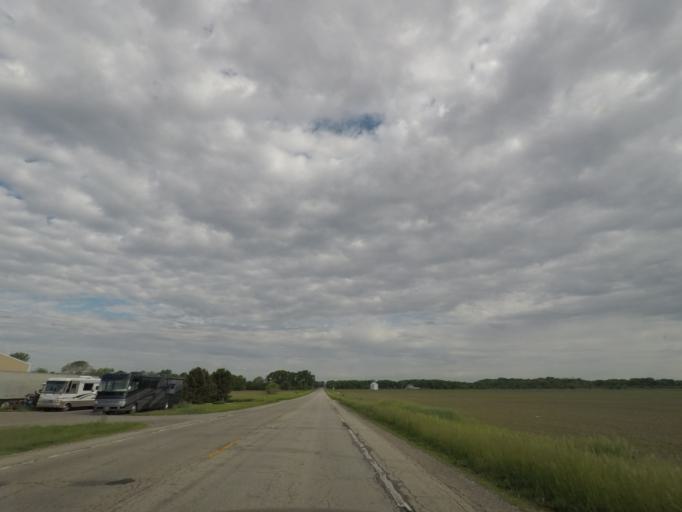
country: US
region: Illinois
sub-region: Logan County
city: Lincoln
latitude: 40.1098
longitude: -89.3268
